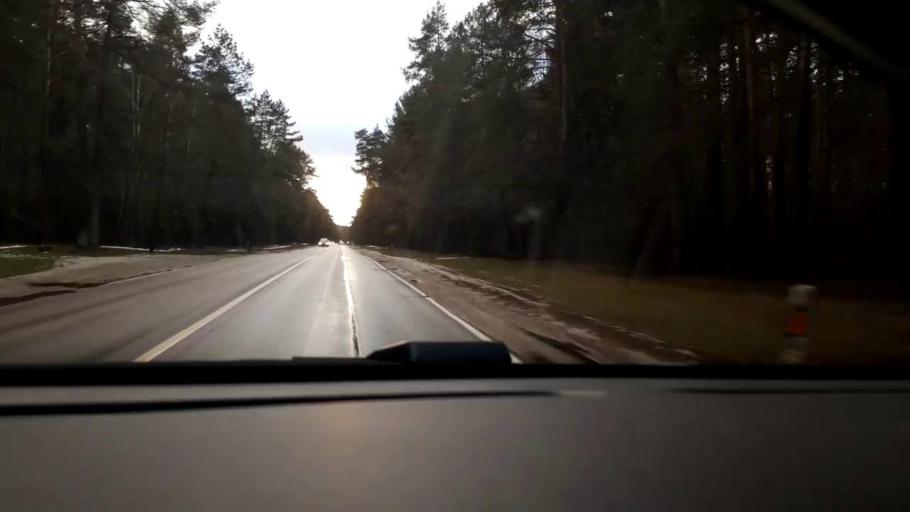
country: LT
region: Vilnius County
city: Rasos
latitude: 54.7699
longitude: 25.3803
